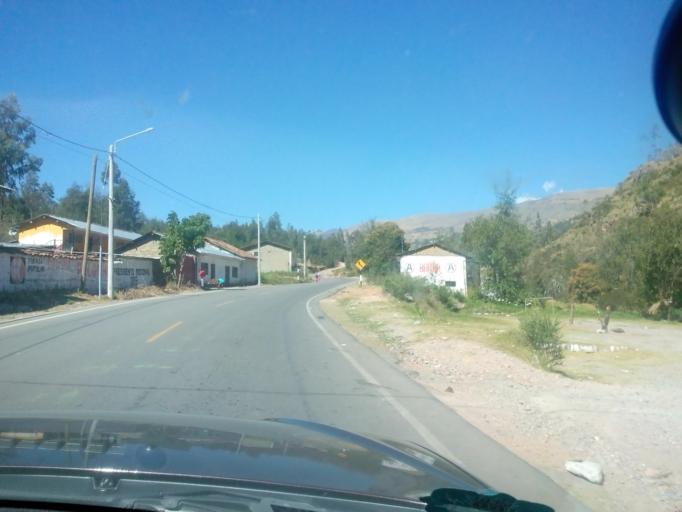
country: PE
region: Apurimac
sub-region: Chincheros
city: Chincheros
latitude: -13.5157
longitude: -73.7044
